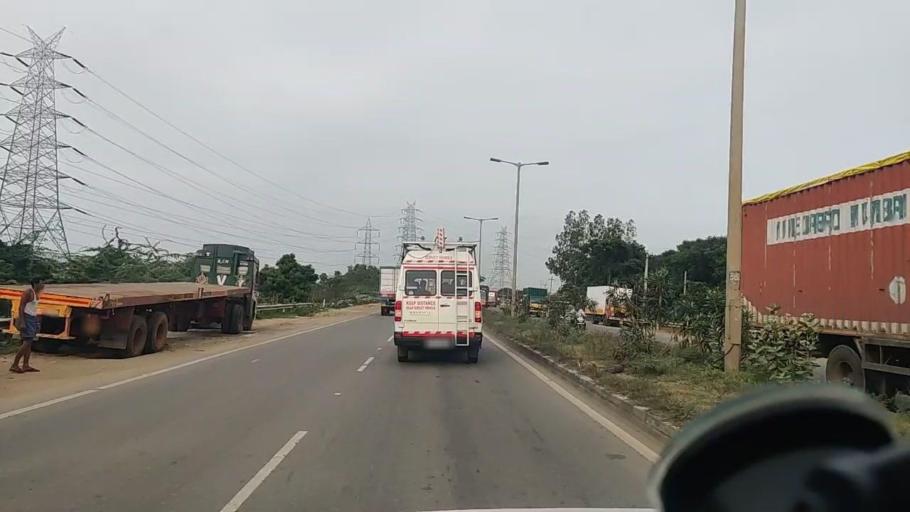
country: IN
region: Tamil Nadu
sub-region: Thiruvallur
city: Manali
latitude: 13.1805
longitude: 80.2577
